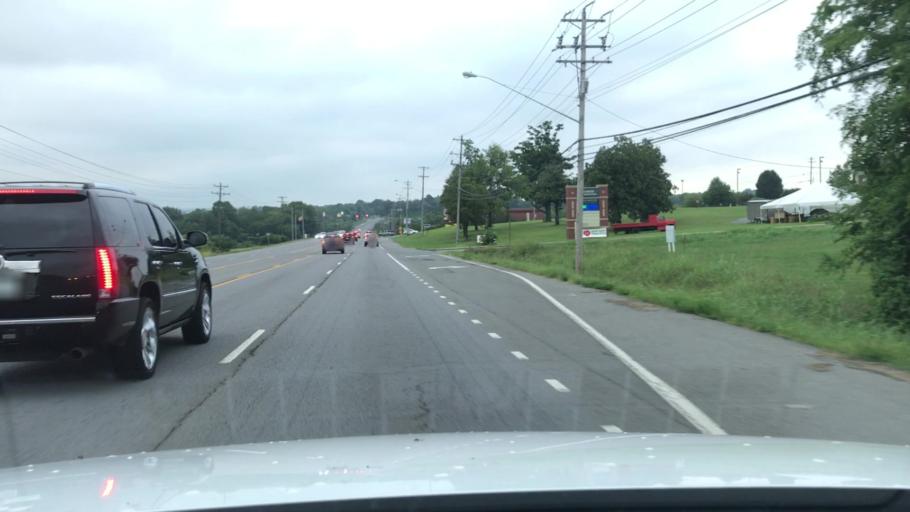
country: US
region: Tennessee
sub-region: Sumner County
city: Gallatin
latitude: 36.3647
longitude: -86.4918
